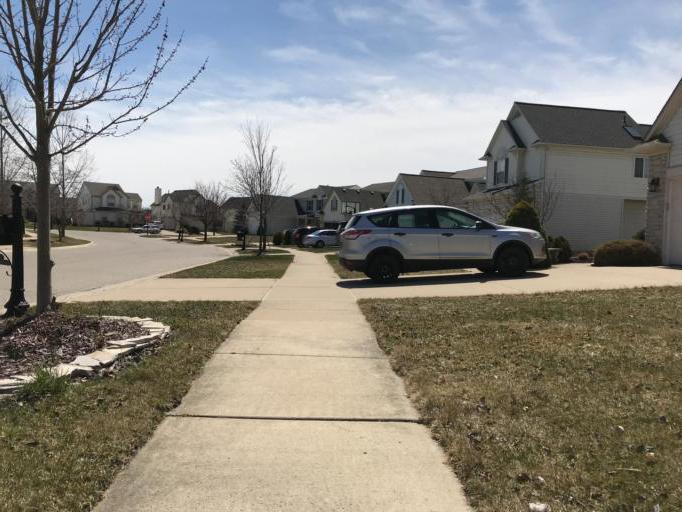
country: US
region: Michigan
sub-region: Washtenaw County
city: Ann Arbor
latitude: 42.2601
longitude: -83.7882
